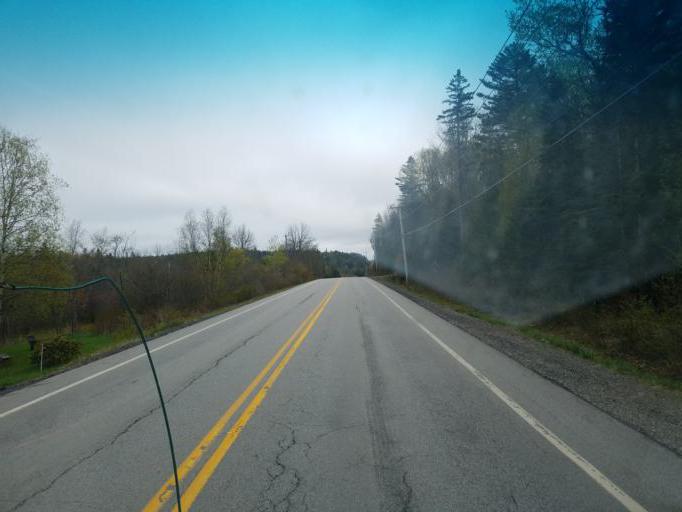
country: US
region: Maine
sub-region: Washington County
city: Eastport
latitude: 44.8060
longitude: -67.0978
